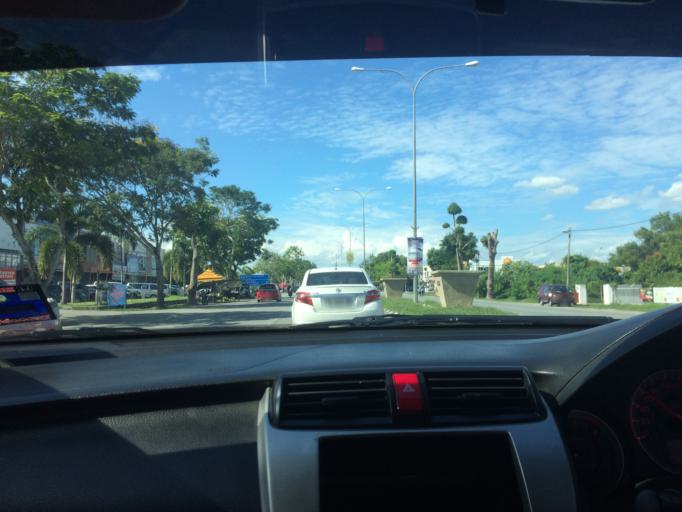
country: MY
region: Kedah
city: Jitra
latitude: 6.2059
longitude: 100.4136
